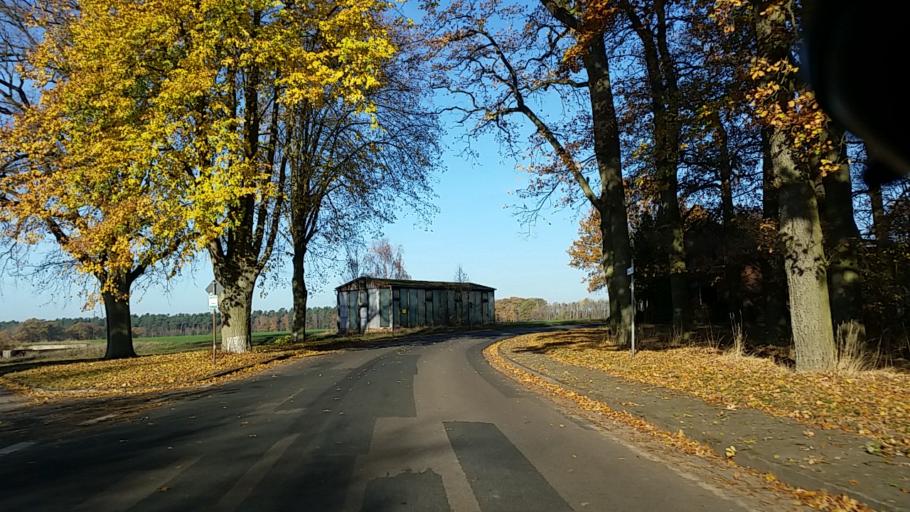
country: DE
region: Lower Saxony
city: Tulau
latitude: 52.6161
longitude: 10.8690
